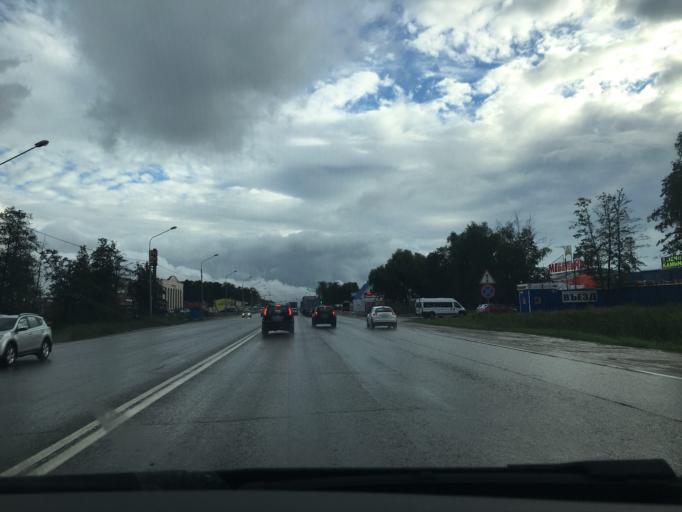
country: RU
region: Kaluga
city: Belousovo
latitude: 55.1113
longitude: 36.6442
